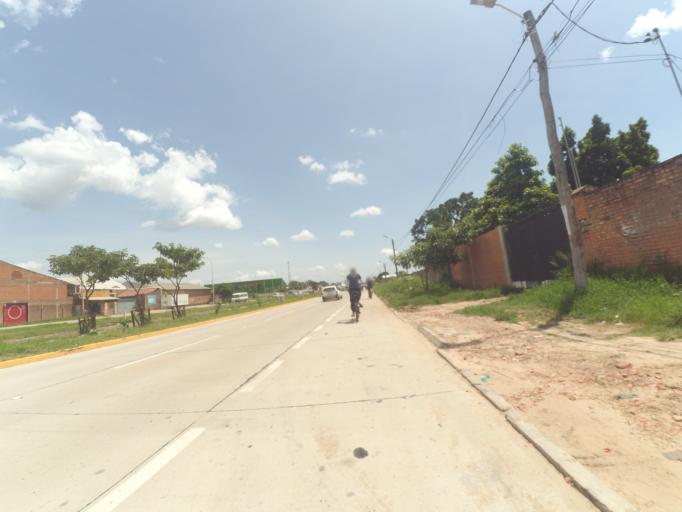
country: BO
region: Santa Cruz
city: Santa Cruz de la Sierra
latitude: -17.7282
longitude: -63.1482
